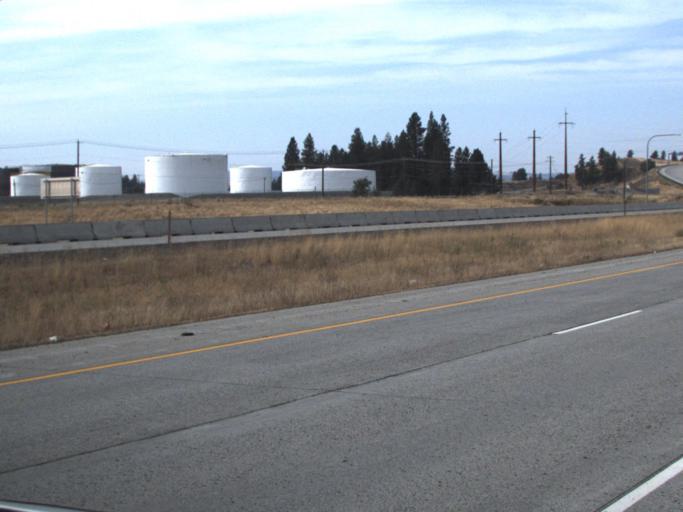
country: US
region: Washington
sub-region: Spokane County
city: Mead
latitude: 47.7584
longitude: -117.3575
